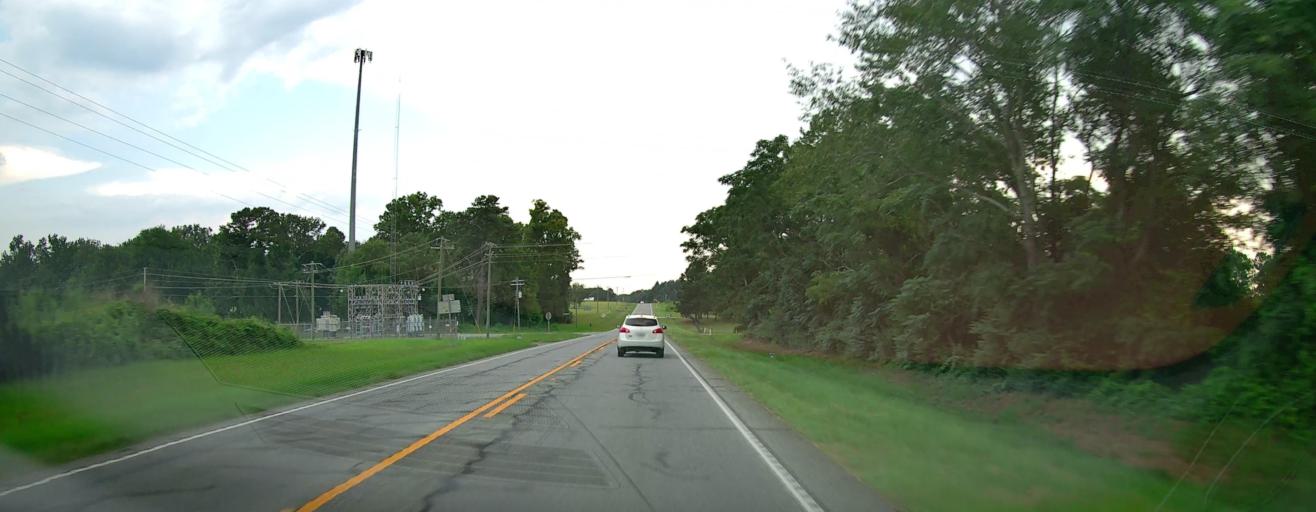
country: US
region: Georgia
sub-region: Laurens County
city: East Dublin
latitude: 32.5688
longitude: -82.8432
